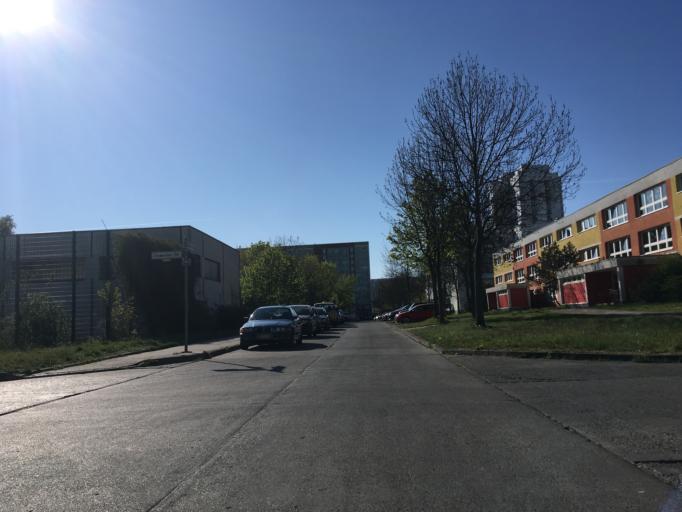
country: DE
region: Berlin
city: Neu-Hohenschoenhausen
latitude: 52.5705
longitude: 13.5127
